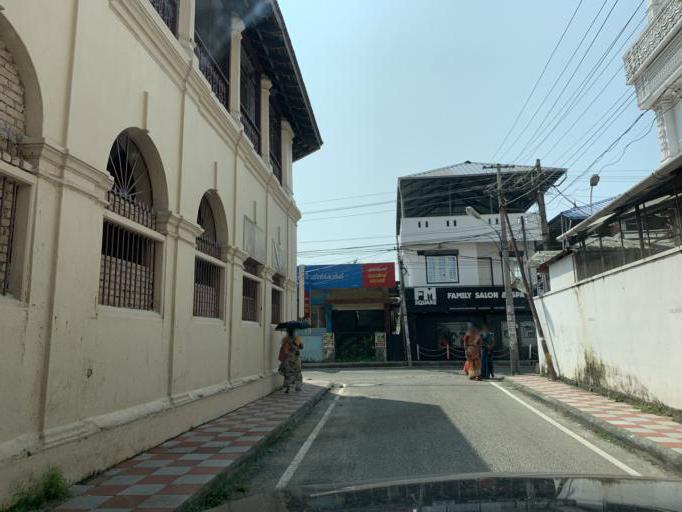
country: IN
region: Kerala
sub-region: Ernakulam
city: Cochin
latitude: 9.9603
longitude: 76.2554
